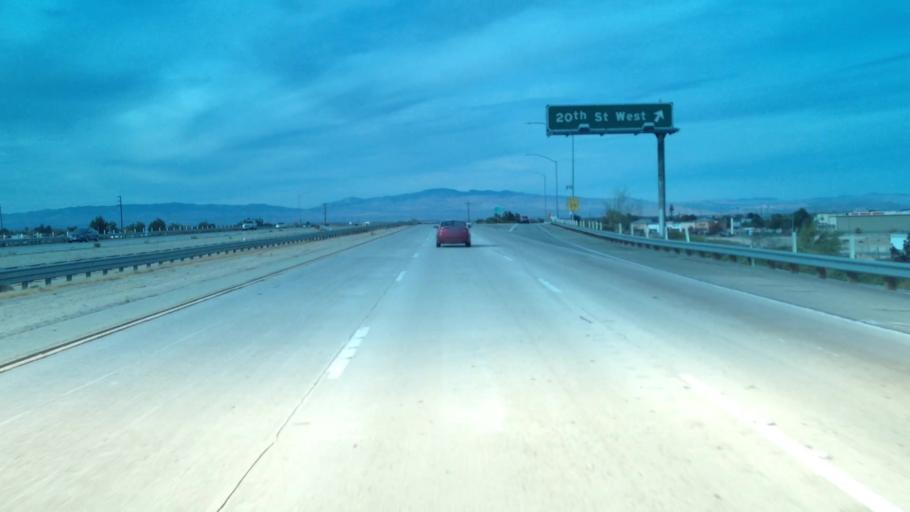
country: US
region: California
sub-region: Los Angeles County
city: Lancaster
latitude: 34.6807
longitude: -118.1628
